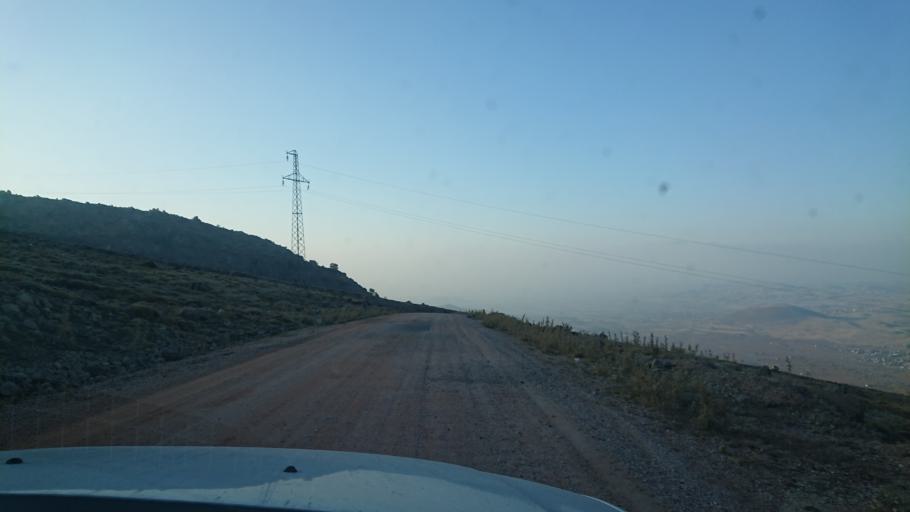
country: TR
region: Aksaray
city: Taspinar
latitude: 38.1621
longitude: 34.1777
